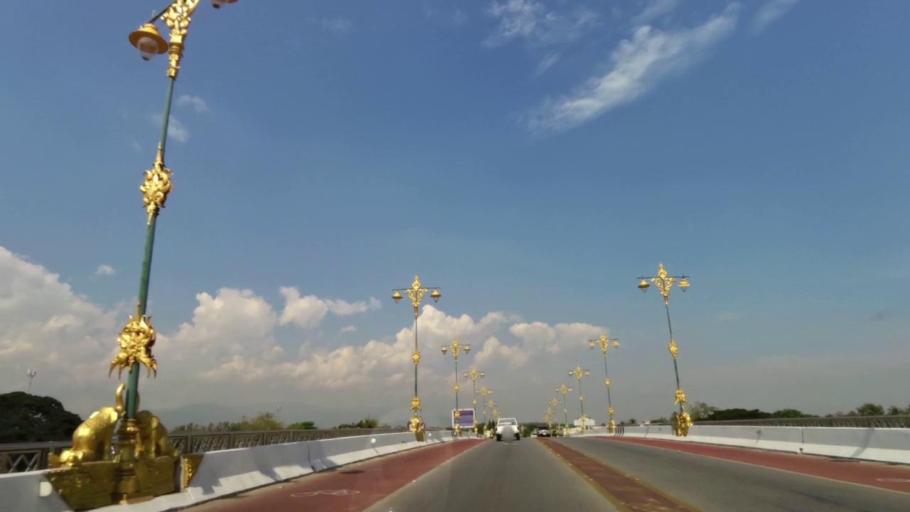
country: TH
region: Chiang Rai
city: Chiang Rai
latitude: 19.9180
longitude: 99.8328
